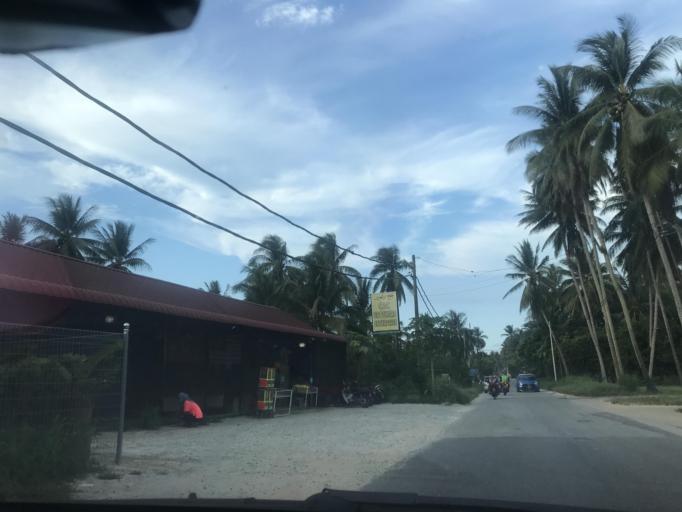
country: MY
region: Kelantan
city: Kota Bharu
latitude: 6.1265
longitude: 102.3568
